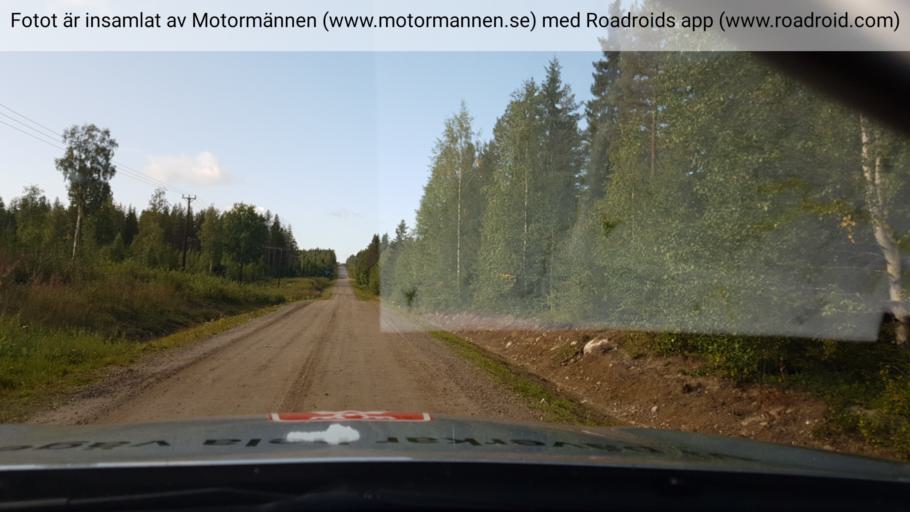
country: SE
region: Norrbotten
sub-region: Kalix Kommun
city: Kalix
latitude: 66.1099
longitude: 23.2955
